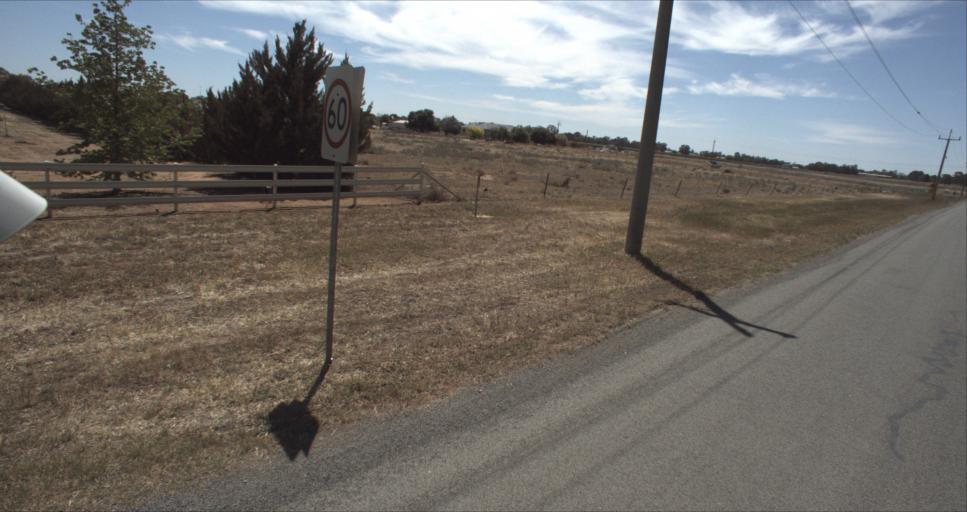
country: AU
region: New South Wales
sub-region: Leeton
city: Leeton
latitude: -34.5746
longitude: 146.4216
